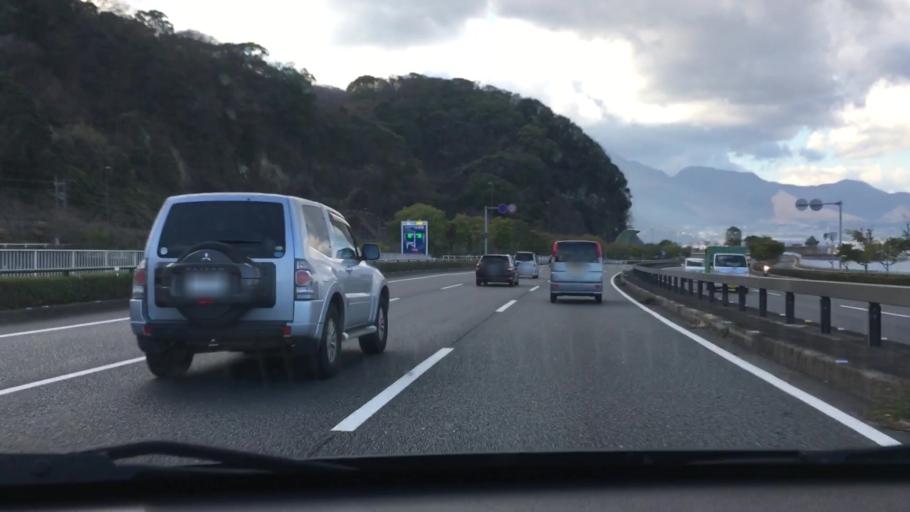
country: JP
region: Oita
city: Oita
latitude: 33.2557
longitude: 131.5574
